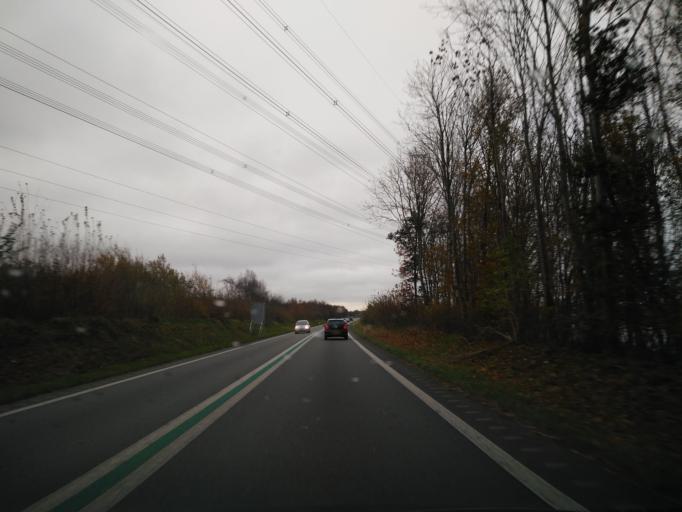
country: NL
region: Drenthe
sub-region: Gemeente Emmen
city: Emmer-Compascuum
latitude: 52.9162
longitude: 7.0372
